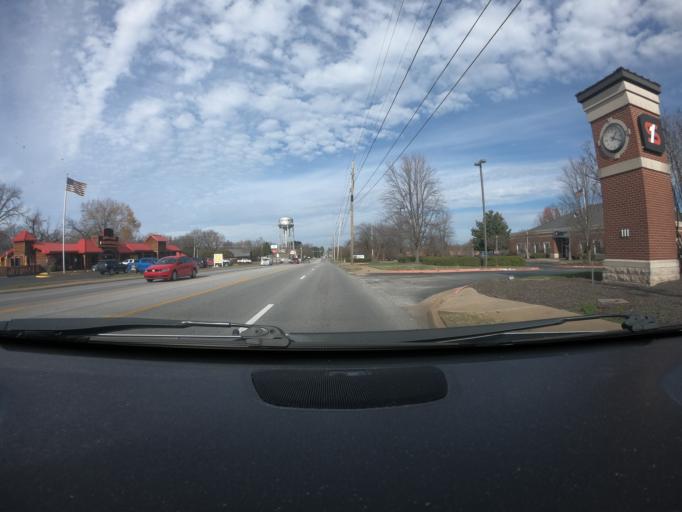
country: US
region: Arkansas
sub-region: Benton County
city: Rogers
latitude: 36.3343
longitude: -94.1258
